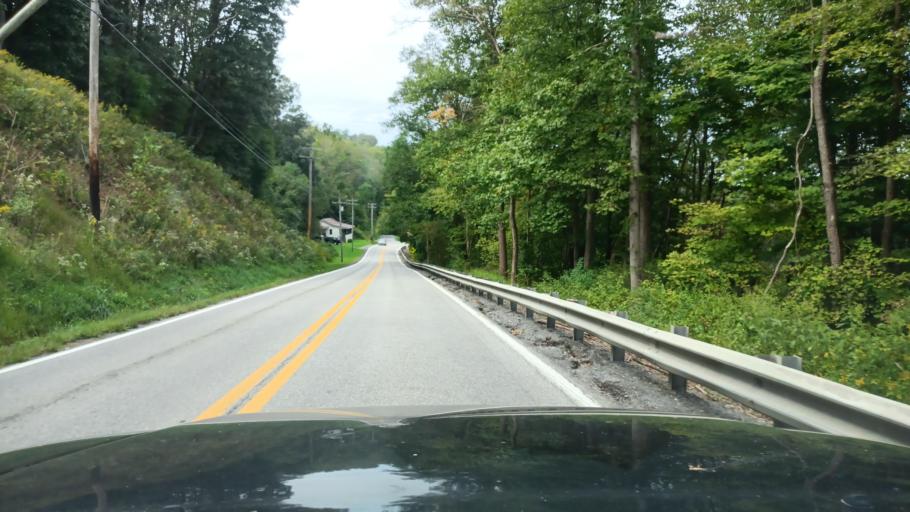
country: US
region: West Virginia
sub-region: Taylor County
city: Grafton
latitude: 39.3444
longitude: -80.0278
